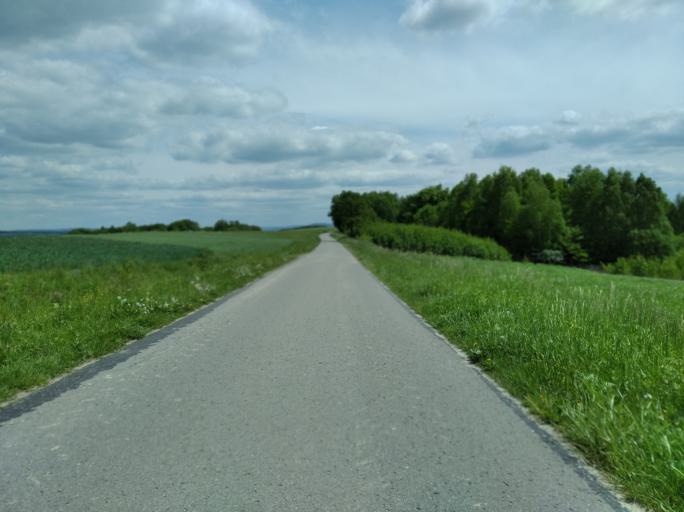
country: PL
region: Subcarpathian Voivodeship
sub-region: Powiat strzyzowski
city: Wisniowa
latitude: 49.8961
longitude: 21.6148
